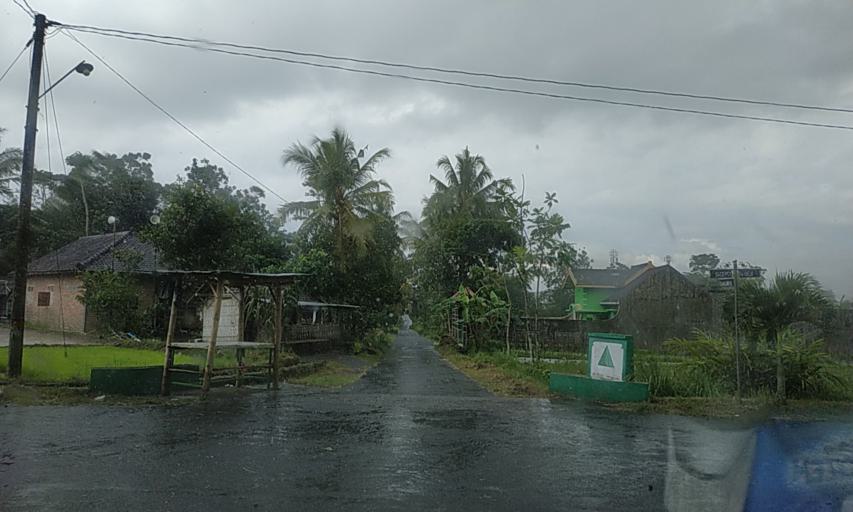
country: ID
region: Daerah Istimewa Yogyakarta
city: Sleman
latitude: -7.6749
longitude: 110.4136
